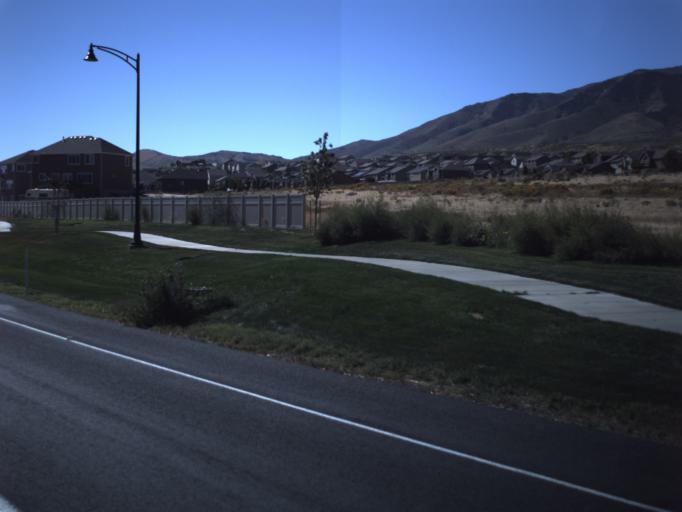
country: US
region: Utah
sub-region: Utah County
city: Saratoga Springs
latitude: 40.3043
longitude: -111.8860
